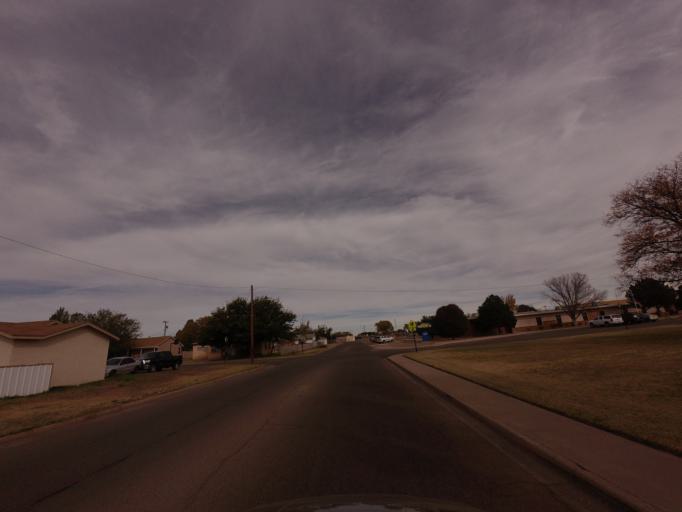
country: US
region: New Mexico
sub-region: Curry County
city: Clovis
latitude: 34.4251
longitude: -103.2070
